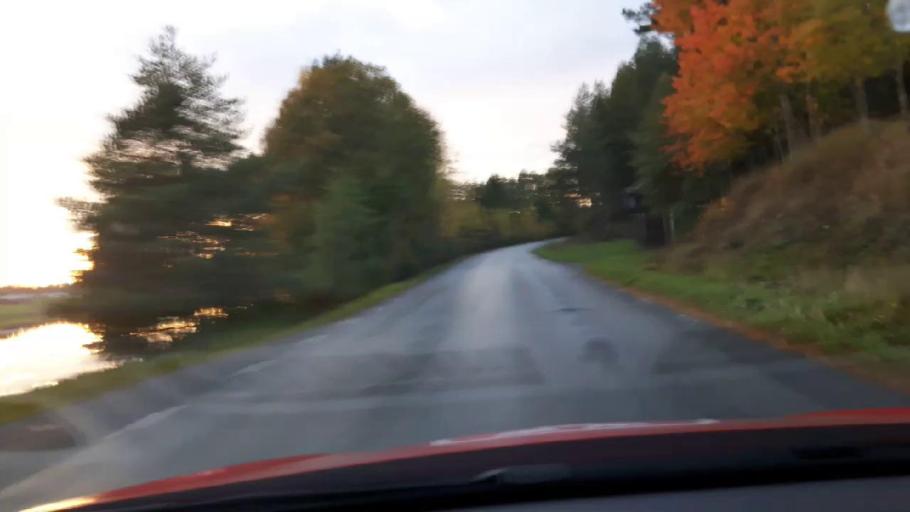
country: SE
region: Jaemtland
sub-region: OEstersunds Kommun
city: Lit
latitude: 63.3202
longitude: 14.9173
